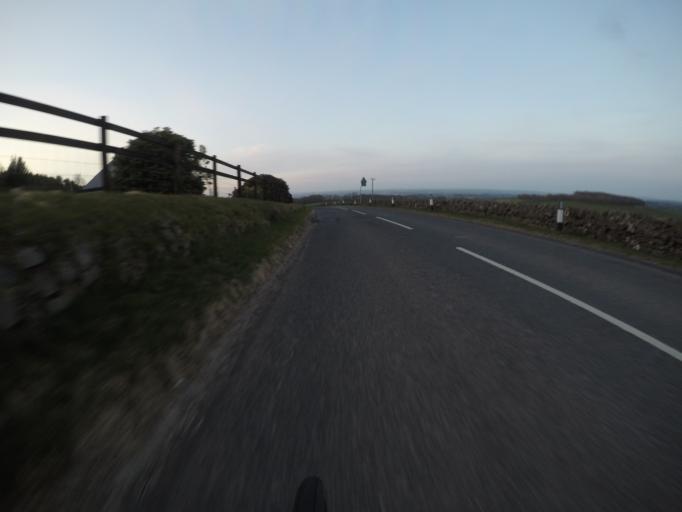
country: GB
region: Scotland
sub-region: South Ayrshire
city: Dundonald
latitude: 55.5648
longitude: -4.6024
